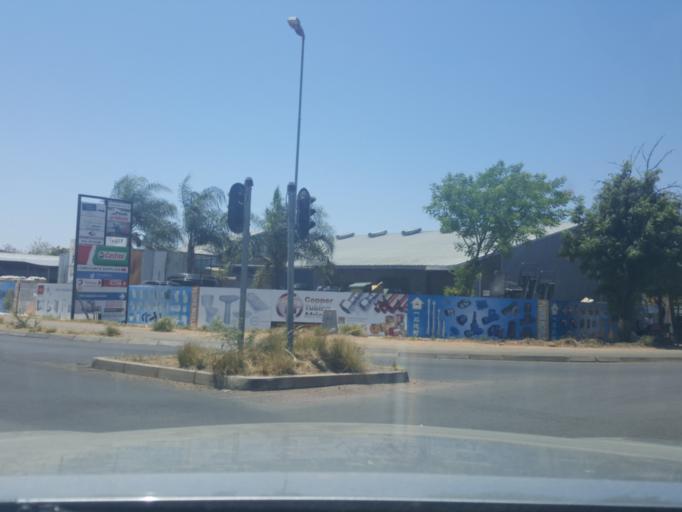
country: BW
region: South East
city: Gaborone
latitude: -24.6800
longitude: 25.8882
